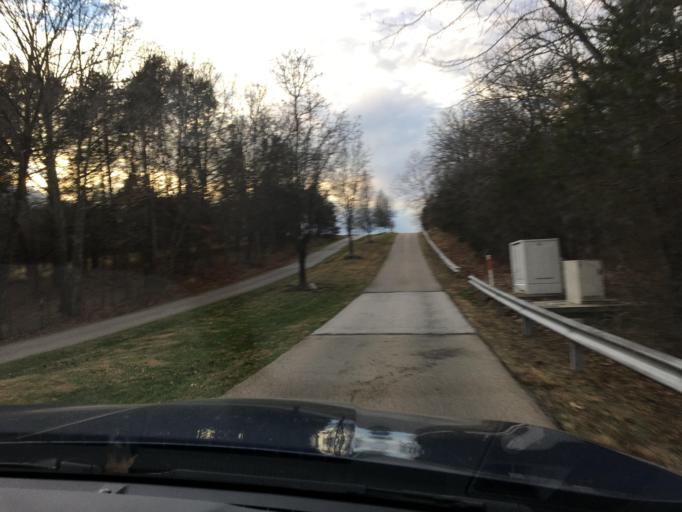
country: US
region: Missouri
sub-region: Jefferson County
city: De Soto
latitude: 38.0914
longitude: -90.5638
